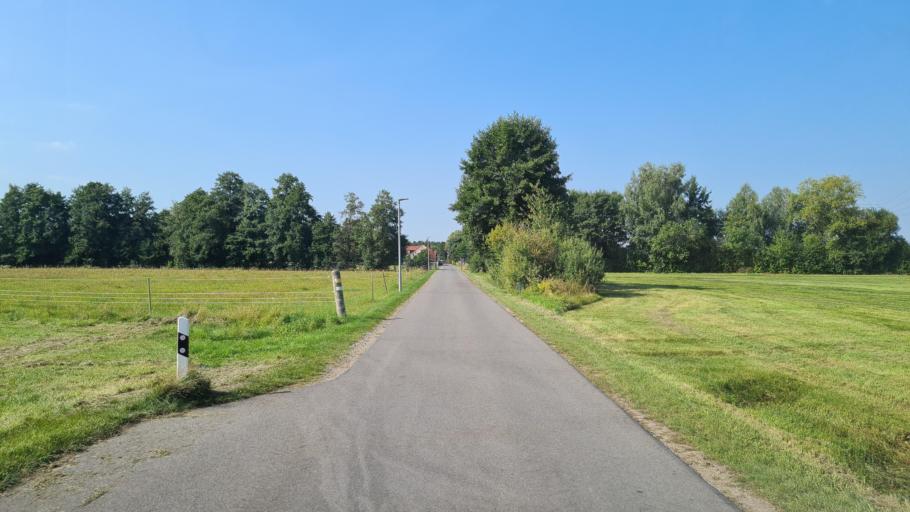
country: DE
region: Brandenburg
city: Kolkwitz
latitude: 51.7433
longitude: 14.2233
